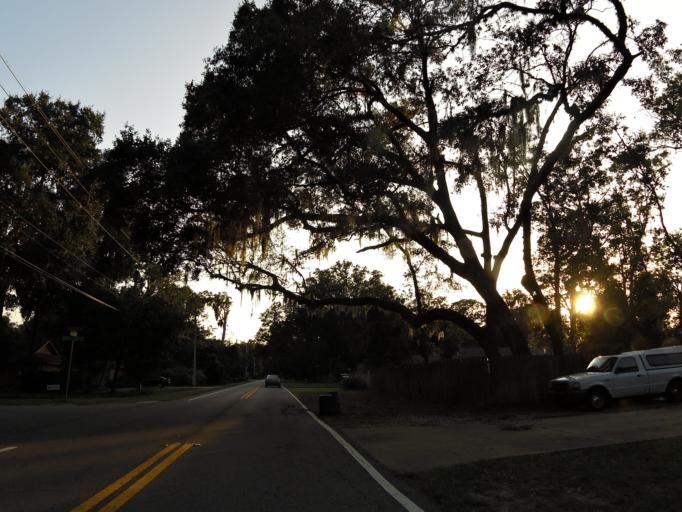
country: US
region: Florida
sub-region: Clay County
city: Orange Park
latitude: 30.2033
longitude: -81.6350
